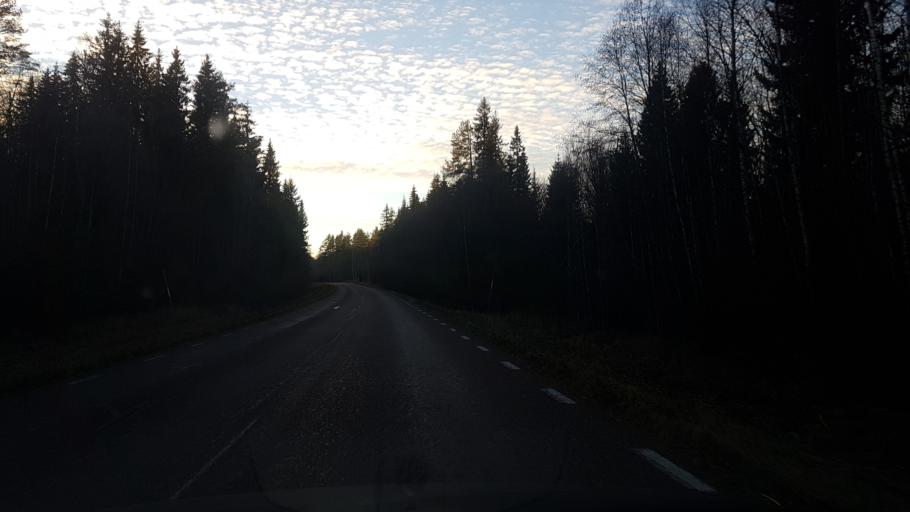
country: SE
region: Dalarna
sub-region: Leksand Municipality
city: Smedby
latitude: 60.7451
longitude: 15.2097
